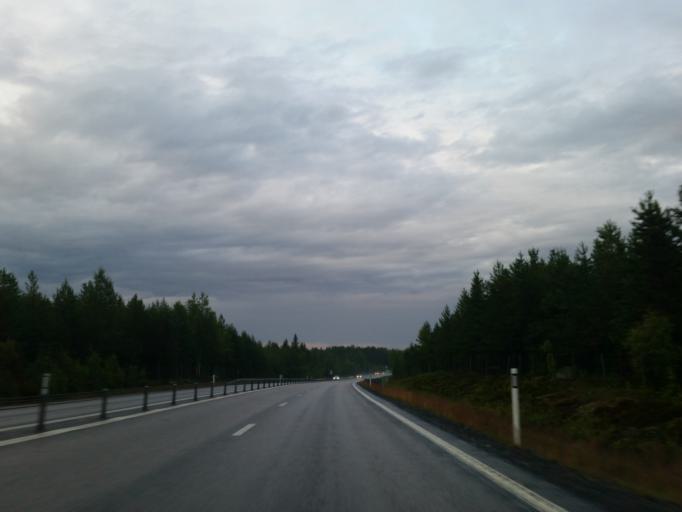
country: SE
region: Vaesterbotten
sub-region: Umea Kommun
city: Saevar
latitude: 63.9857
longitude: 20.7367
